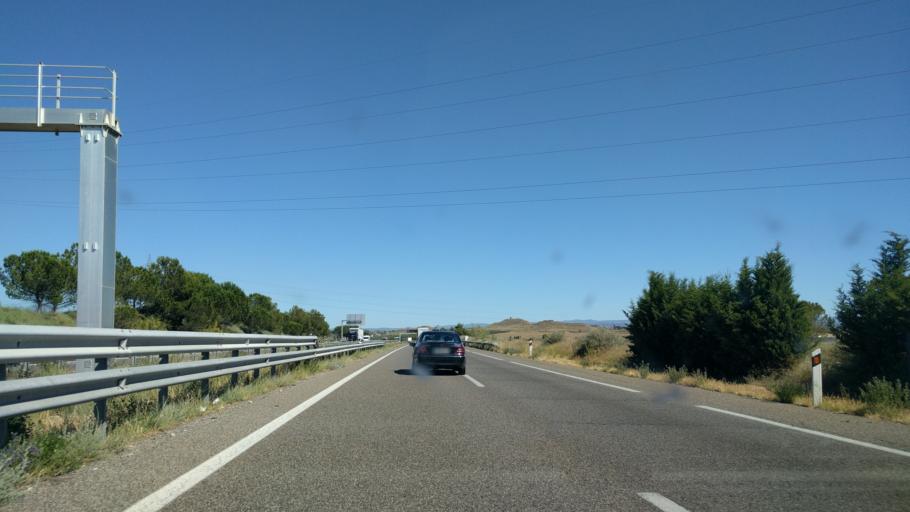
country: ES
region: Catalonia
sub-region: Provincia de Lleida
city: Alcoletge
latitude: 41.6342
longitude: 0.6909
